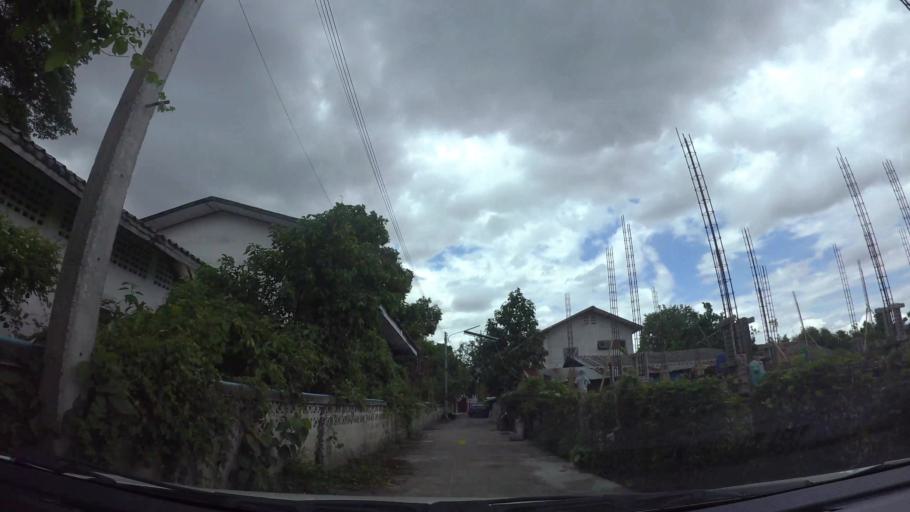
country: TH
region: Chiang Mai
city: Saraphi
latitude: 18.7507
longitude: 99.0390
